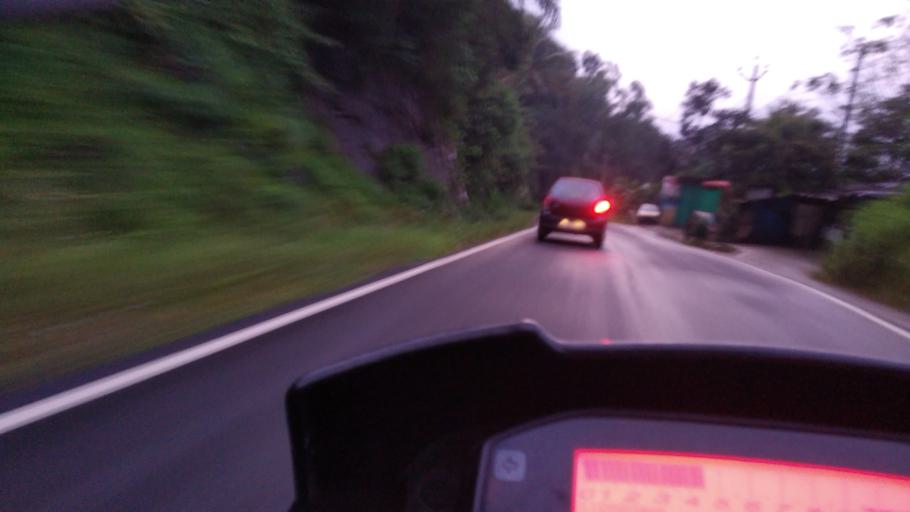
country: IN
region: Kerala
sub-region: Idukki
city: Munnar
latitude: 9.9606
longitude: 77.0730
